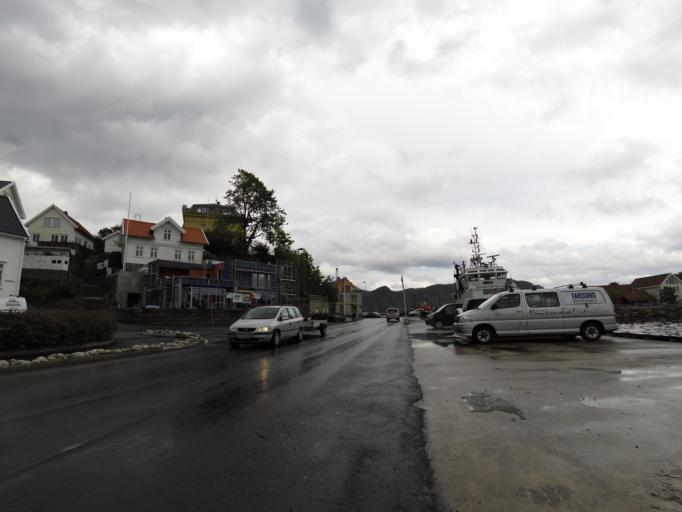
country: NO
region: Vest-Agder
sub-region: Farsund
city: Farsund
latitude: 58.0923
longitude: 6.8054
